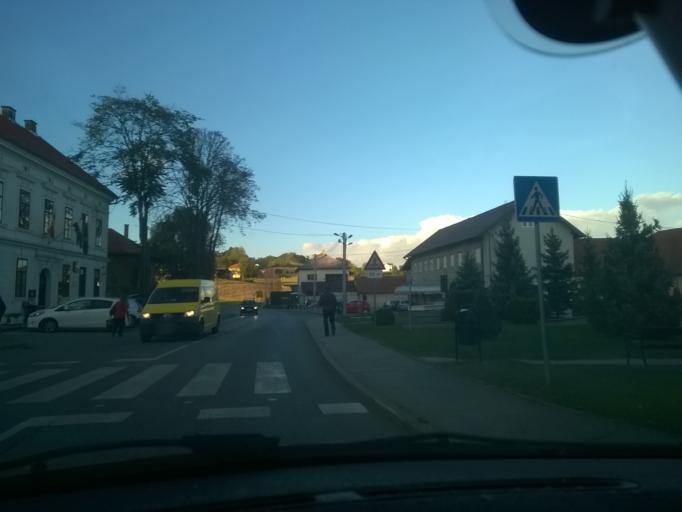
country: HR
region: Zagrebacka
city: Jakovlje
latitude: 46.0022
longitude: 15.8445
